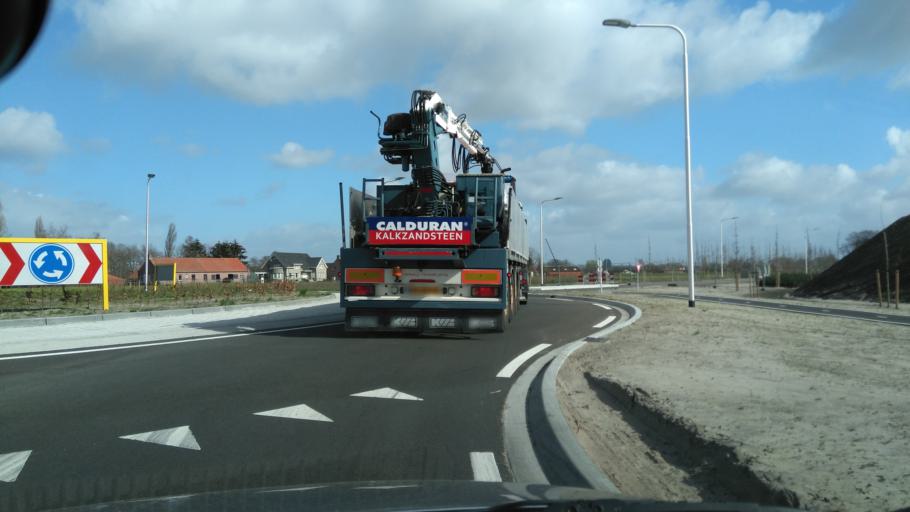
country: NL
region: North Brabant
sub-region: Gemeente Baarle-Nassau
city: Baarle-Nassau
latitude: 51.4288
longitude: 4.9331
